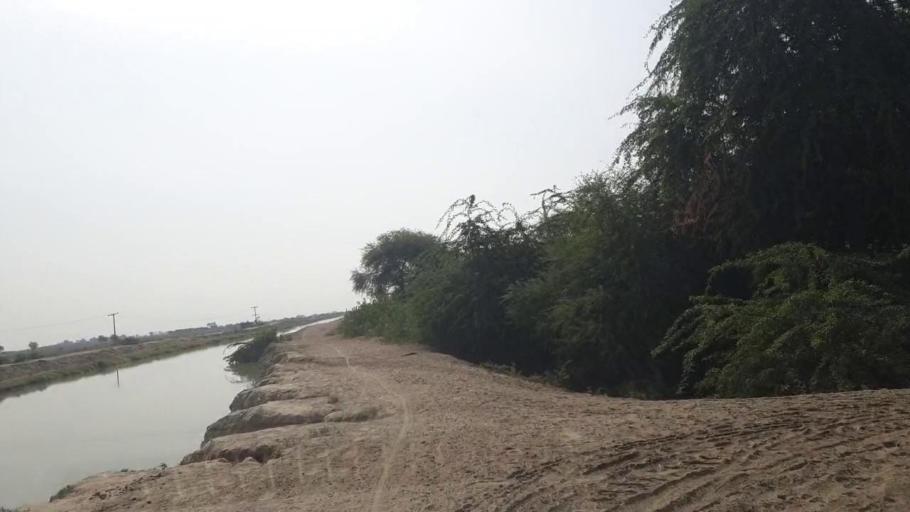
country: PK
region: Sindh
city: Badin
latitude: 24.5514
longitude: 68.8499
